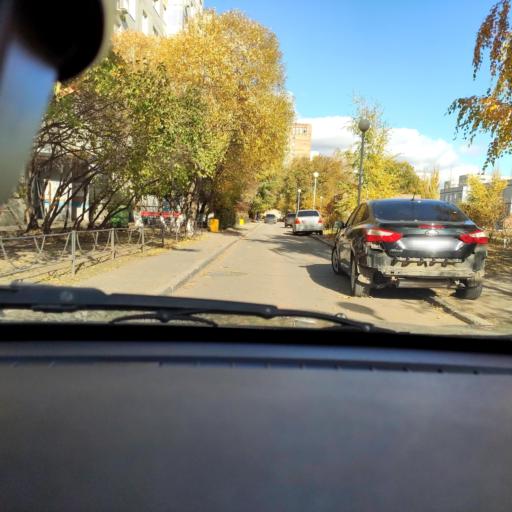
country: RU
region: Samara
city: Tol'yatti
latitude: 53.5429
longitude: 49.3320
